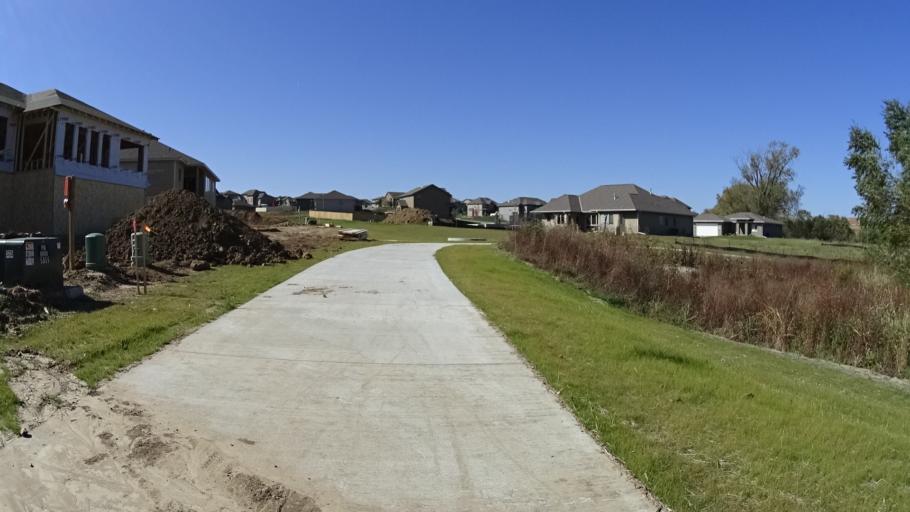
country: US
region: Nebraska
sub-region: Sarpy County
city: La Vista
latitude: 41.1664
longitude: -96.0153
